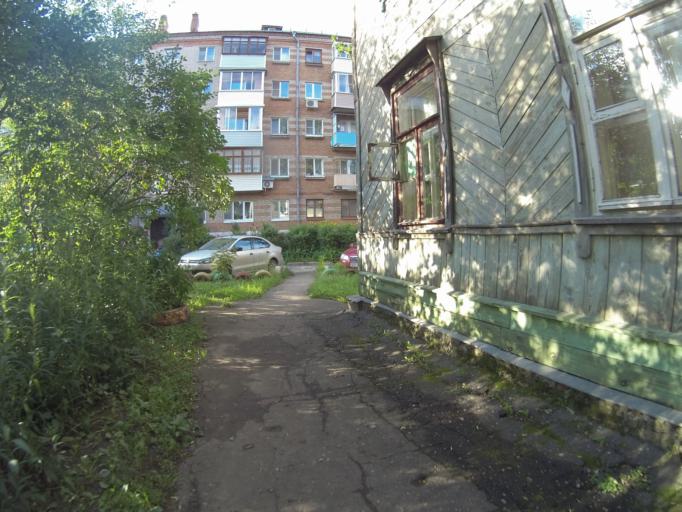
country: RU
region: Vladimir
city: Vladimir
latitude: 56.1487
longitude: 40.4245
